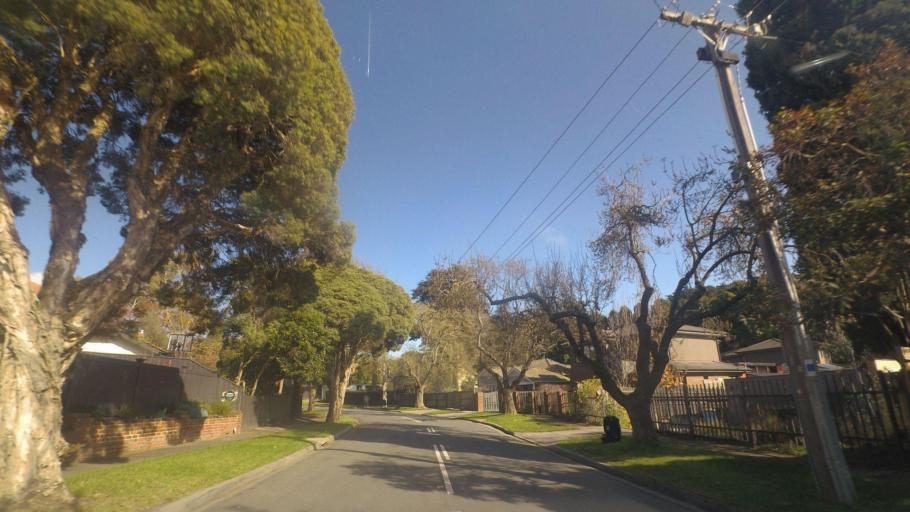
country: AU
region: Victoria
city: Mont Albert
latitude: -37.8109
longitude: 145.1023
